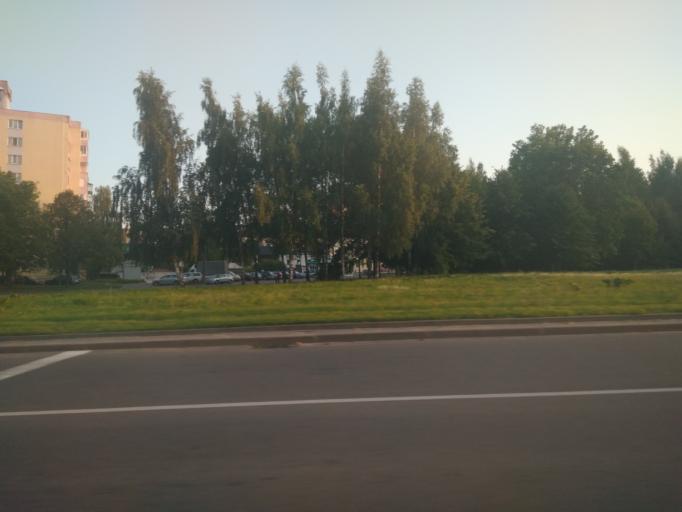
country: BY
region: Minsk
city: Novoye Medvezhino
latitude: 53.9289
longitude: 27.4825
